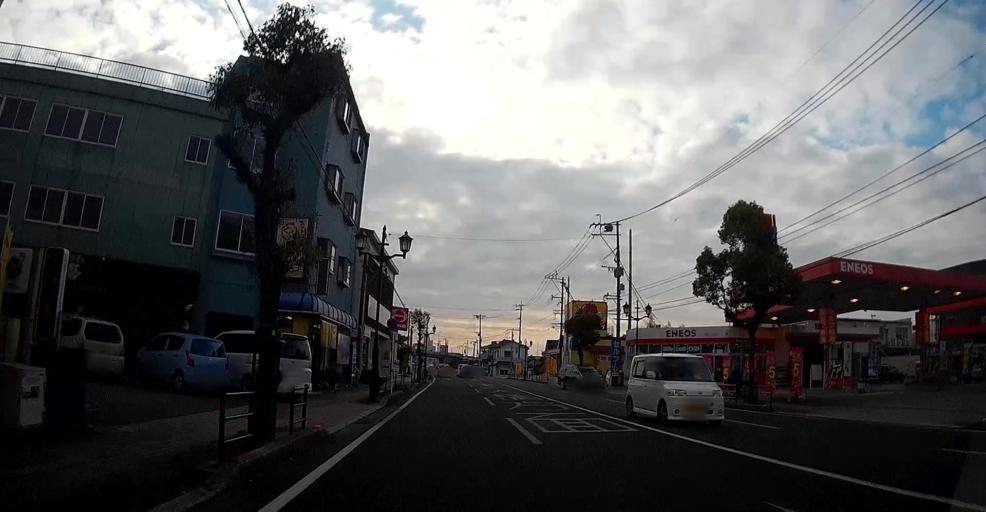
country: JP
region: Kumamoto
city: Hondo
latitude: 32.4488
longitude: 130.1997
